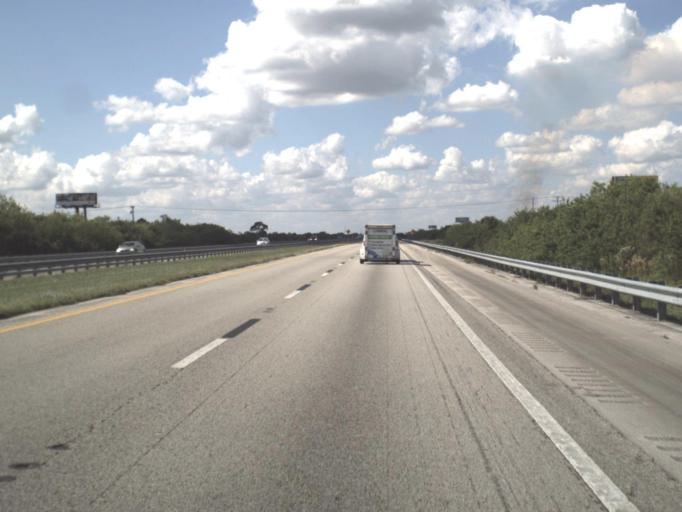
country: US
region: Florida
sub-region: Saint Lucie County
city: Lakewood Park
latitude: 27.4846
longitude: -80.4698
